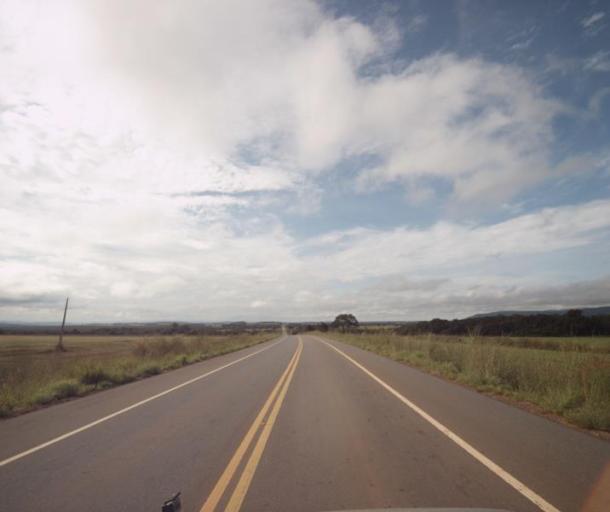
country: BR
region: Goias
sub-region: Barro Alto
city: Barro Alto
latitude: -15.2947
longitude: -48.6760
